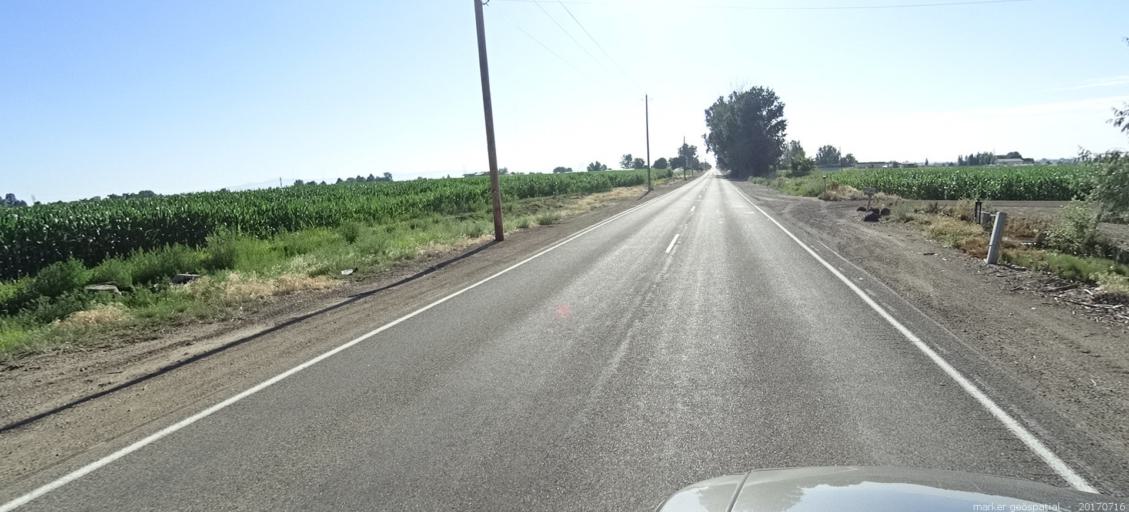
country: US
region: Idaho
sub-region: Ada County
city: Kuna
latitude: 43.5465
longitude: -116.4217
